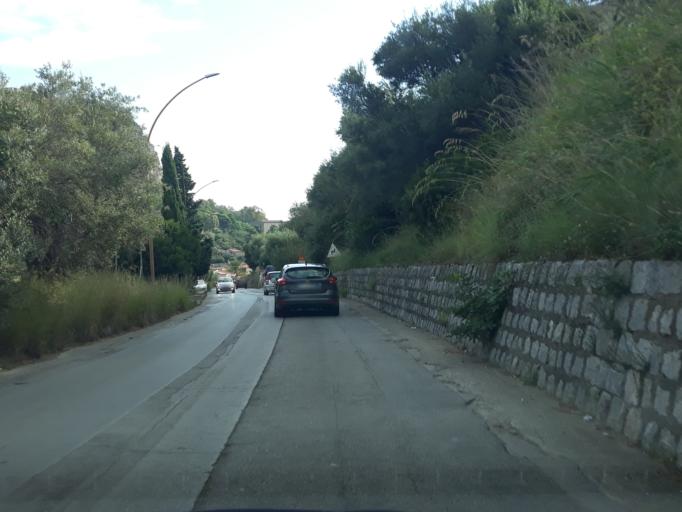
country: IT
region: Sicily
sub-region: Palermo
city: Cefalu
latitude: 38.0305
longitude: 14.0208
